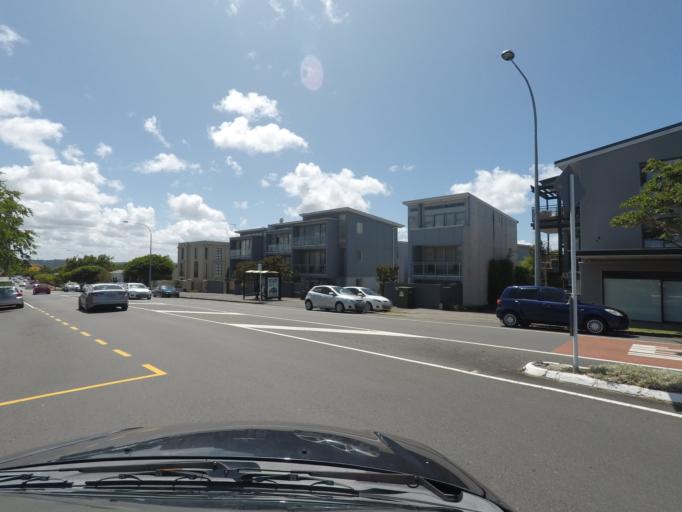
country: NZ
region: Auckland
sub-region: Auckland
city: Auckland
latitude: -36.8613
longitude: 174.7247
